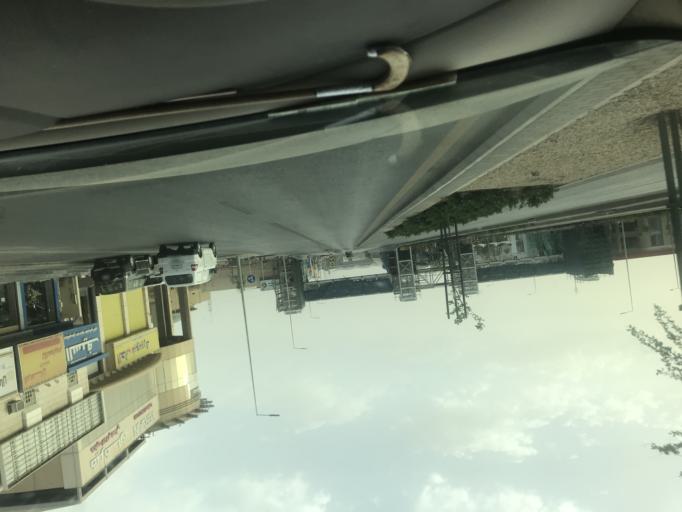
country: SA
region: Ar Riyad
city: Riyadh
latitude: 24.7780
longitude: 46.6645
